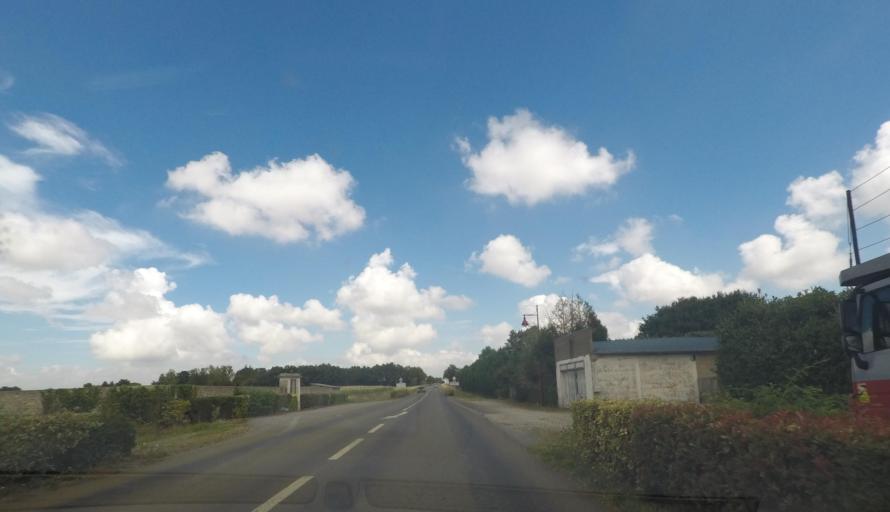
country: FR
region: Pays de la Loire
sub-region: Departement de la Sarthe
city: Bonnetable
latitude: 48.2292
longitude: 0.4315
